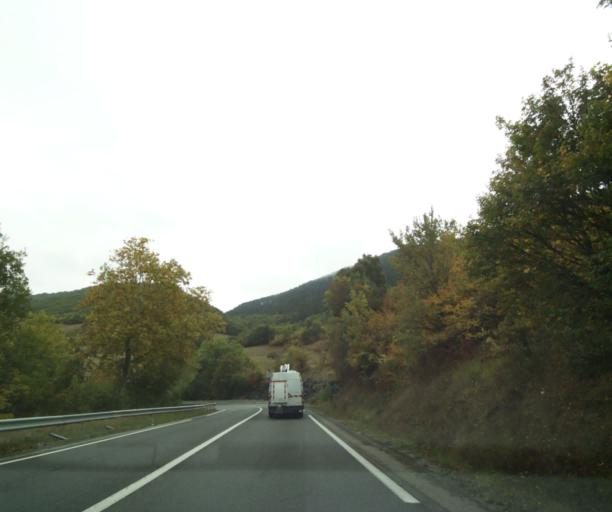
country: FR
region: Midi-Pyrenees
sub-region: Departement de l'Aveyron
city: Millau
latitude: 44.0873
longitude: 3.0869
